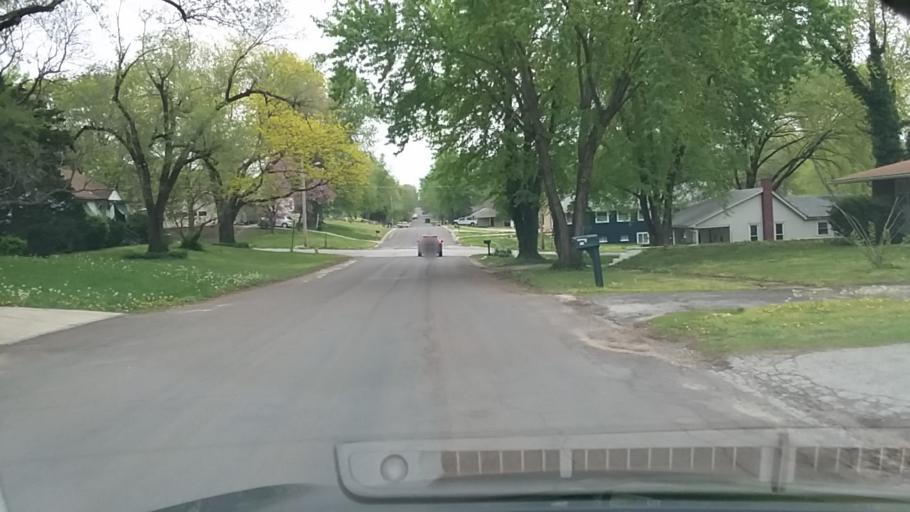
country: US
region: Kansas
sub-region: Douglas County
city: Eudora
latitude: 38.9410
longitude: -95.0989
